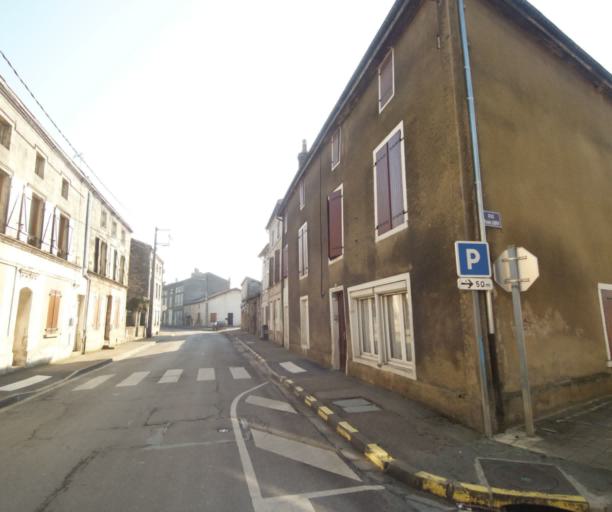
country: FR
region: Champagne-Ardenne
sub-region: Departement de la Haute-Marne
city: Wassy
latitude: 48.4967
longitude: 4.9502
